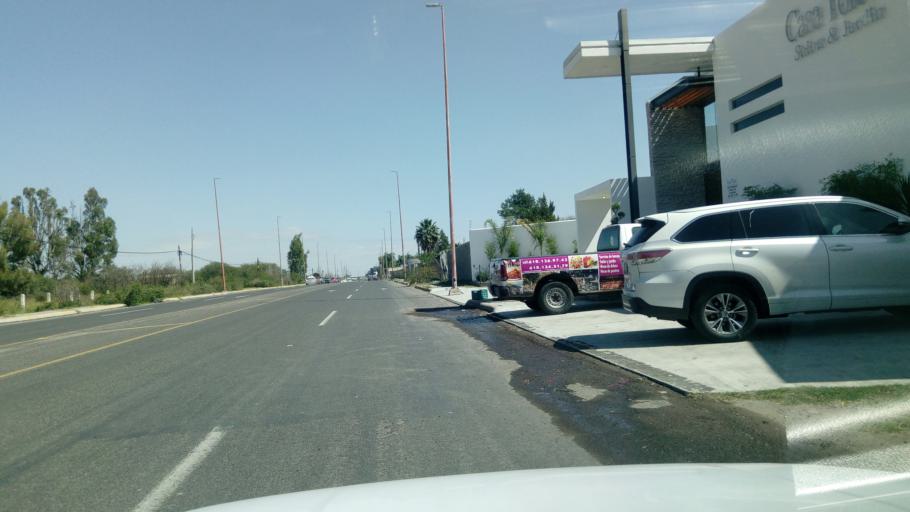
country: MX
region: Durango
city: Victoria de Durango
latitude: 23.9699
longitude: -104.7037
